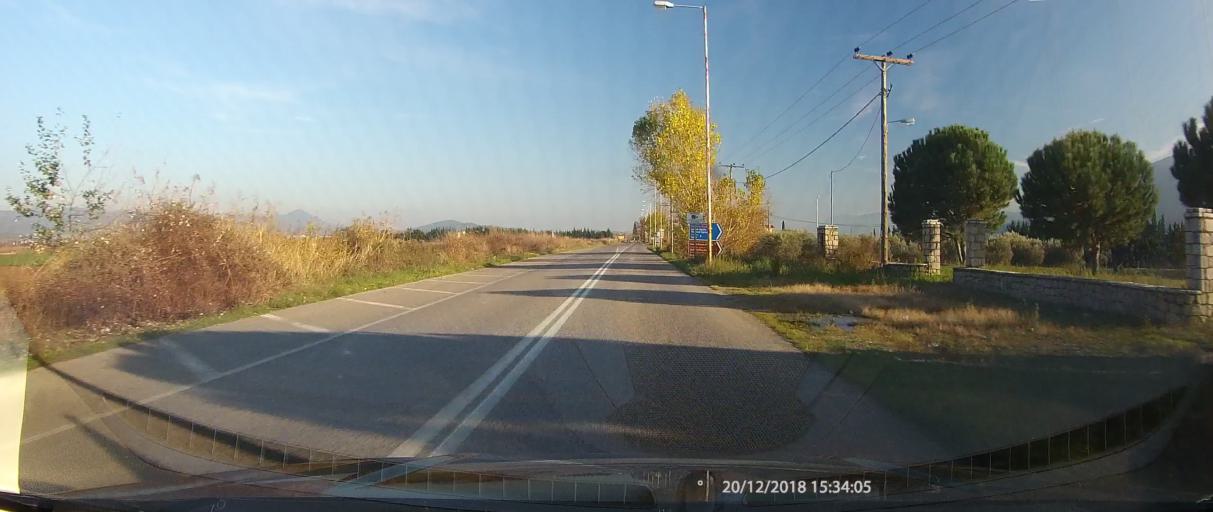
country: GR
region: Central Greece
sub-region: Nomos Fthiotidos
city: Lianokladhion
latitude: 38.9204
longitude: 22.2890
